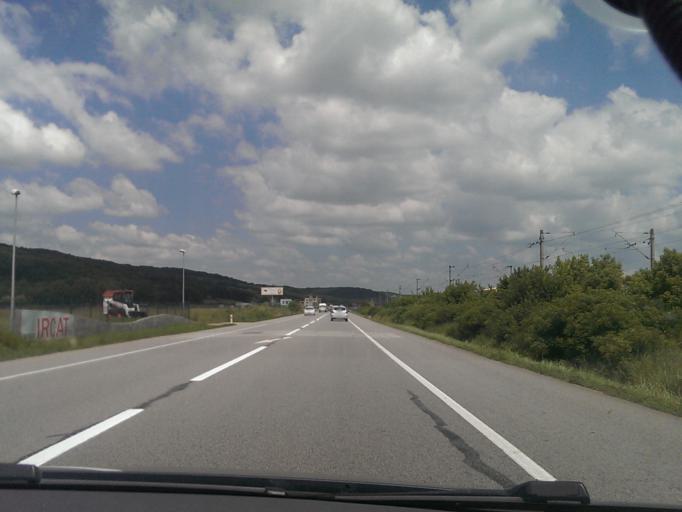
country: RO
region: Cluj
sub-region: Comuna Apahida
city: Apahida
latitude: 46.8305
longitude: 23.7457
